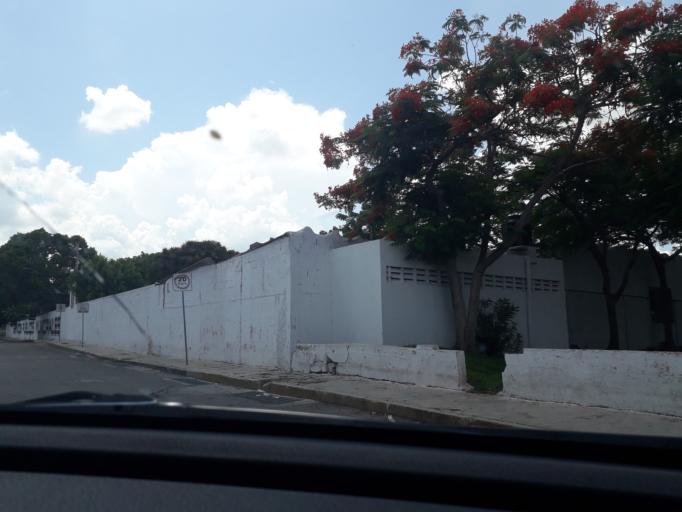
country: MX
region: Yucatan
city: Merida
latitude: 20.9820
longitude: -89.6550
